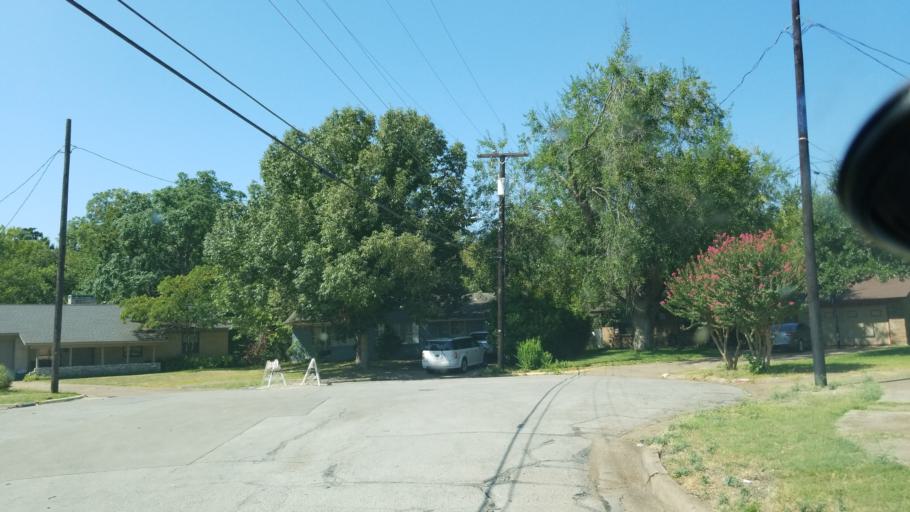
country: US
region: Texas
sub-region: Dallas County
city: Duncanville
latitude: 32.6553
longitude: -96.9006
